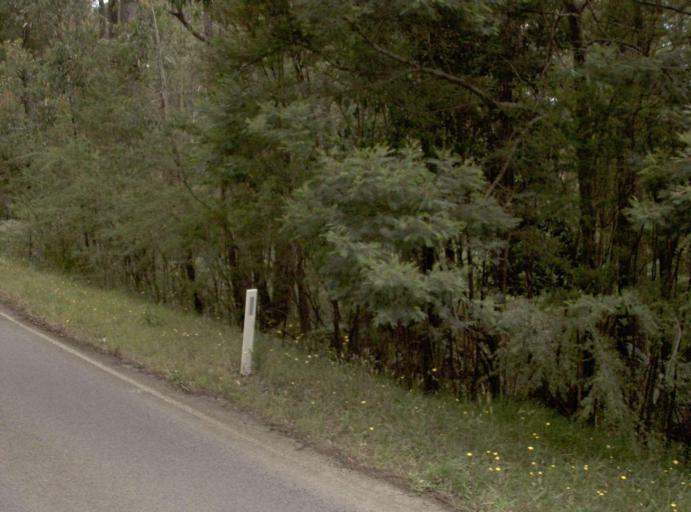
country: AU
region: Victoria
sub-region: Latrobe
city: Traralgon
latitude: -38.0887
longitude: 146.4381
